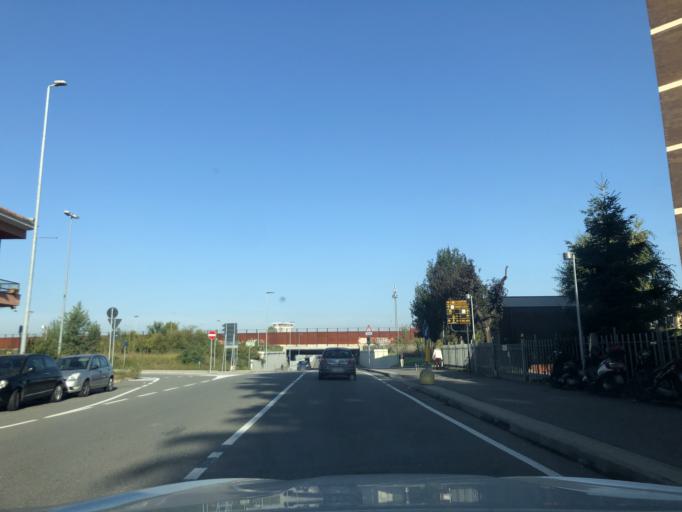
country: IT
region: Lombardy
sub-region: Citta metropolitana di Milano
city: Baranzate
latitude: 45.5286
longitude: 9.1110
